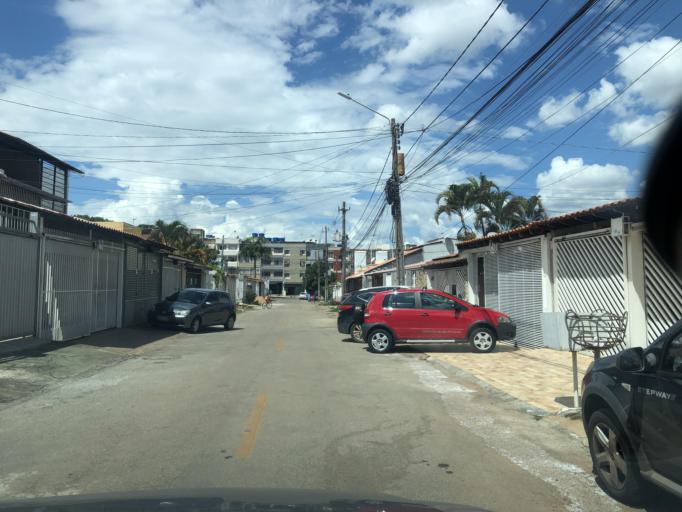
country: BR
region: Federal District
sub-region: Brasilia
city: Brasilia
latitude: -15.8754
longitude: -47.9792
